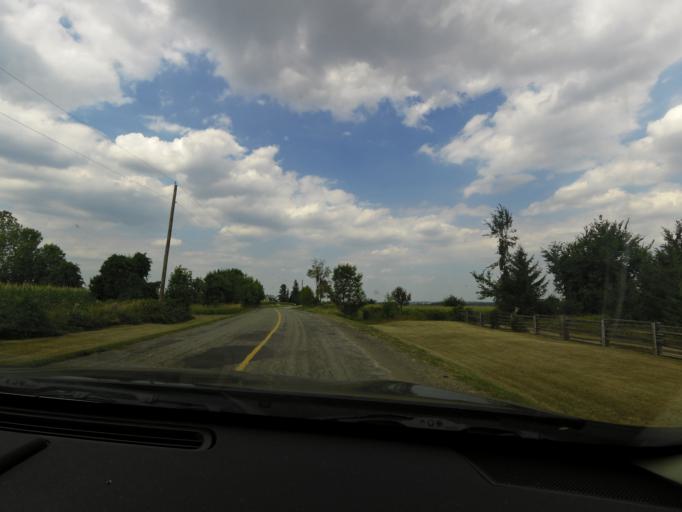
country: CA
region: Ontario
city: Brampton
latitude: 43.7585
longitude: -79.9430
